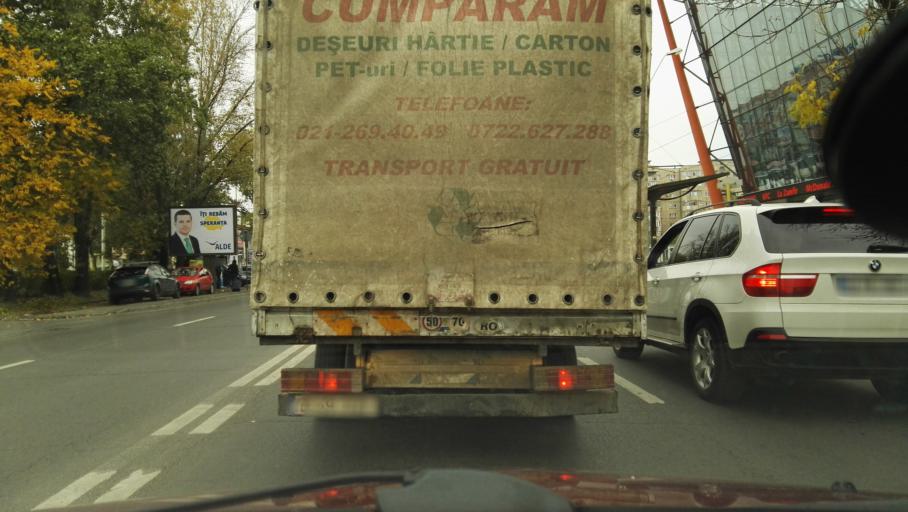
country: RO
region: Bucuresti
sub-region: Municipiul Bucuresti
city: Bucuresti
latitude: 44.4149
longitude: 26.0792
